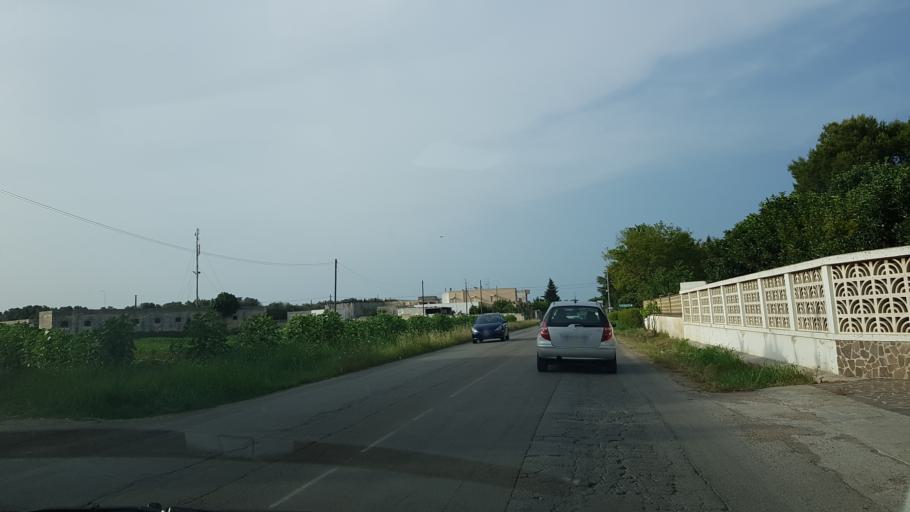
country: IT
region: Apulia
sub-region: Provincia di Brindisi
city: San Pietro Vernotico
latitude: 40.4937
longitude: 17.9903
